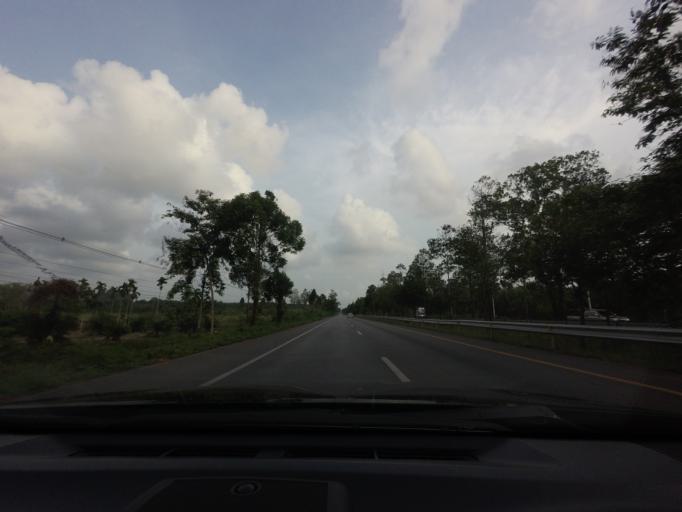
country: TH
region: Chumphon
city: Lamae
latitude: 9.8211
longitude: 99.0623
